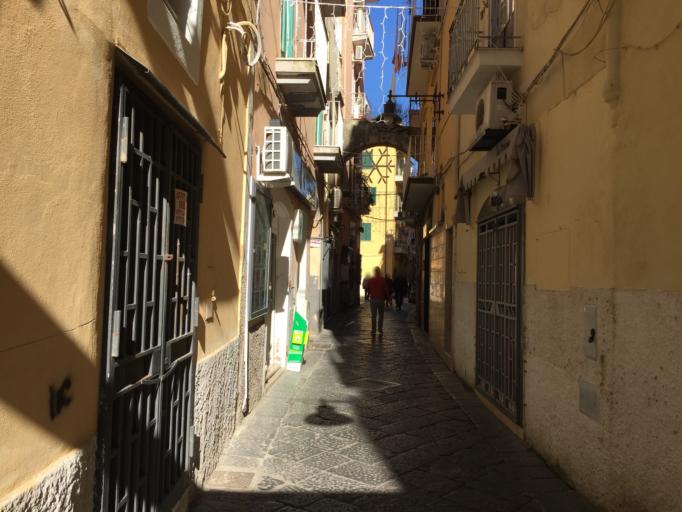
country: IT
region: Latium
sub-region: Provincia di Latina
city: Gaeta
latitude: 41.2155
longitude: 13.5705
